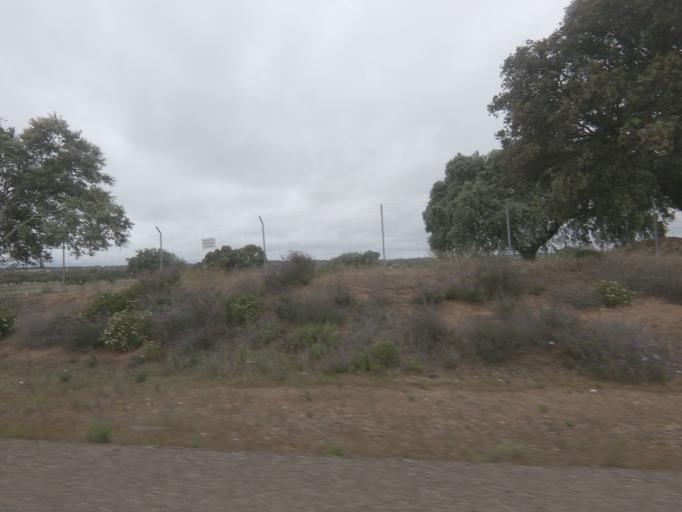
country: ES
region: Extremadura
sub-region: Provincia de Badajoz
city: Villar del Rey
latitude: 39.0161
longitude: -6.8512
